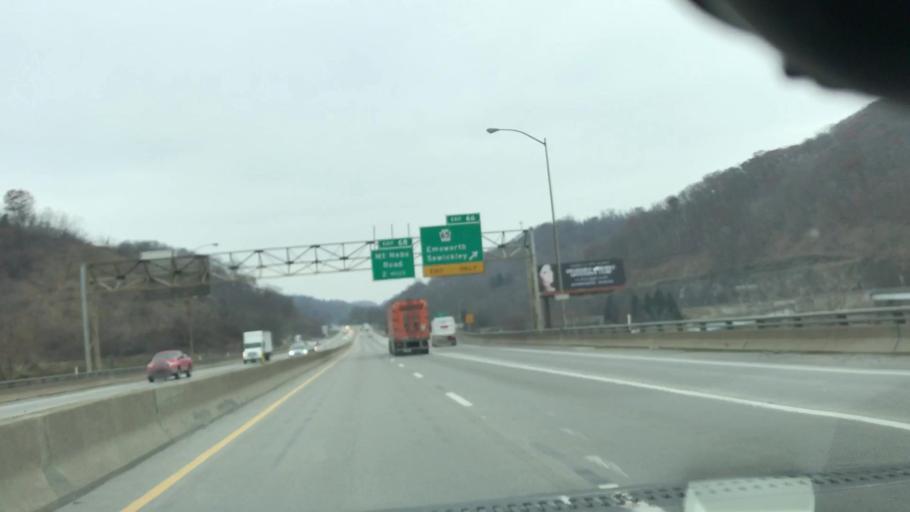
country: US
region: Pennsylvania
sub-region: Allegheny County
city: Coraopolis
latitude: 40.5165
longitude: -80.1335
